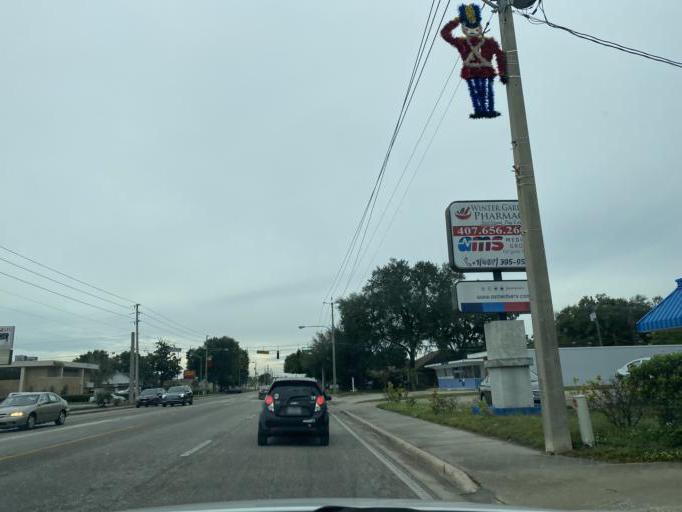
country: US
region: Florida
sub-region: Orange County
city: Winter Garden
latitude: 28.5554
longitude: -81.5836
